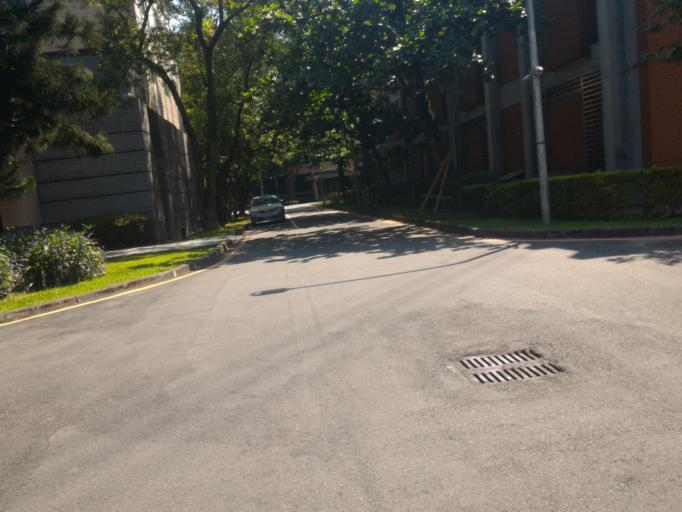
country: TW
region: Taipei
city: Taipei
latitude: 25.0406
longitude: 121.6155
